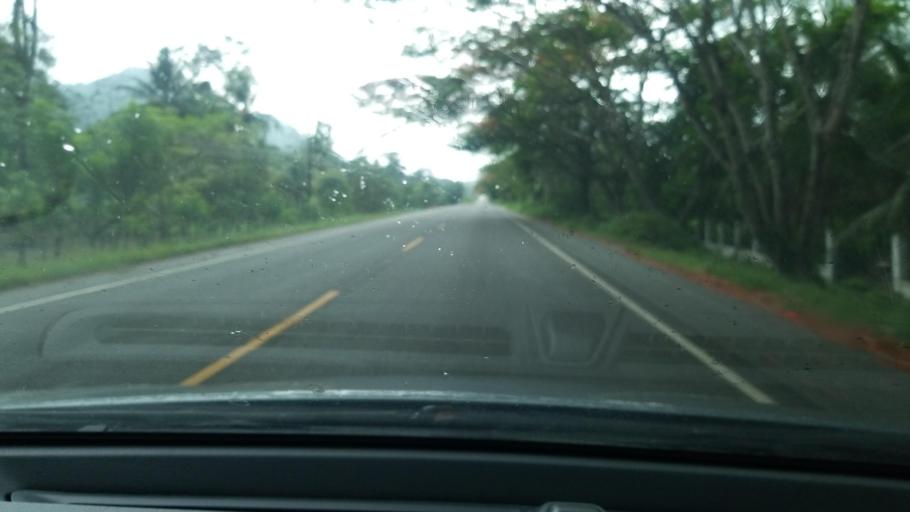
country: HN
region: Cortes
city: Rio Chiquito
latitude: 15.6225
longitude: -88.2641
